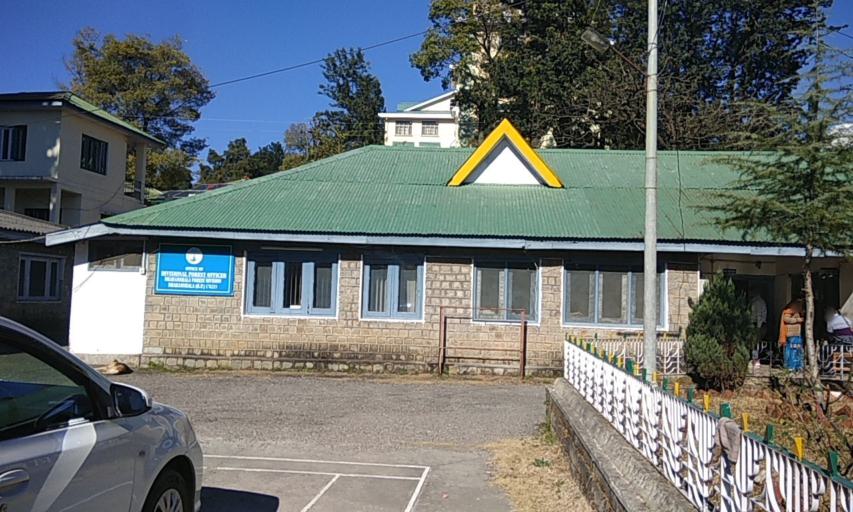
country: IN
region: Himachal Pradesh
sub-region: Kangra
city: Dharmsala
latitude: 32.2104
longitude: 76.3206
